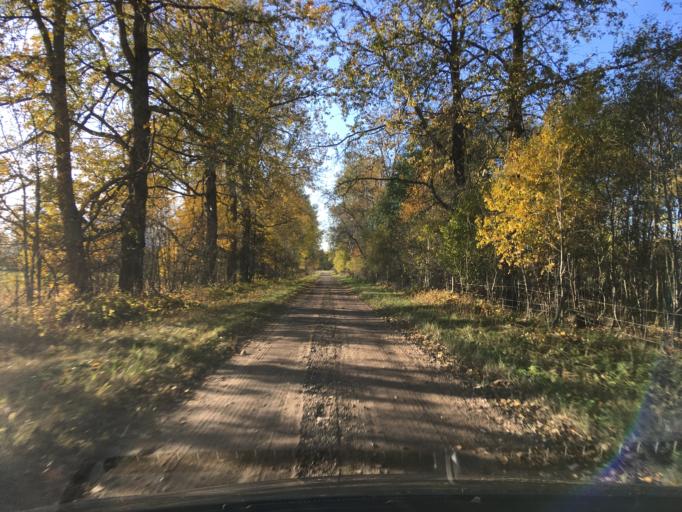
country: EE
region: Laeaene
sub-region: Lihula vald
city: Lihula
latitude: 58.5647
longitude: 23.7914
